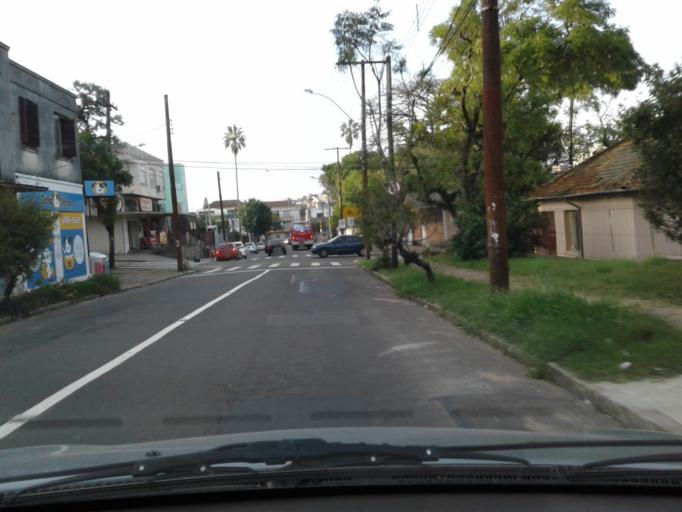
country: BR
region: Rio Grande do Sul
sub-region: Porto Alegre
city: Porto Alegre
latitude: -30.0706
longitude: -51.2105
